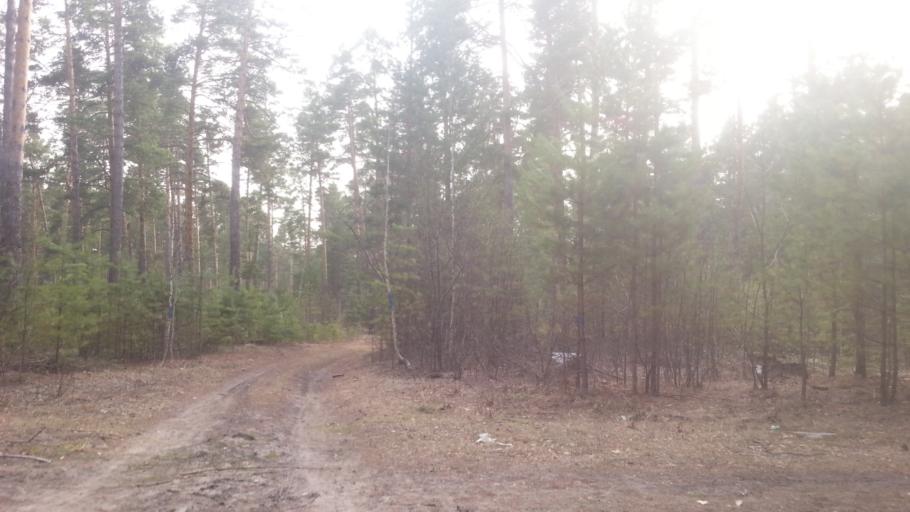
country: RU
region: Altai Krai
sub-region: Gorod Barnaulskiy
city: Barnaul
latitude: 53.3242
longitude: 83.7186
